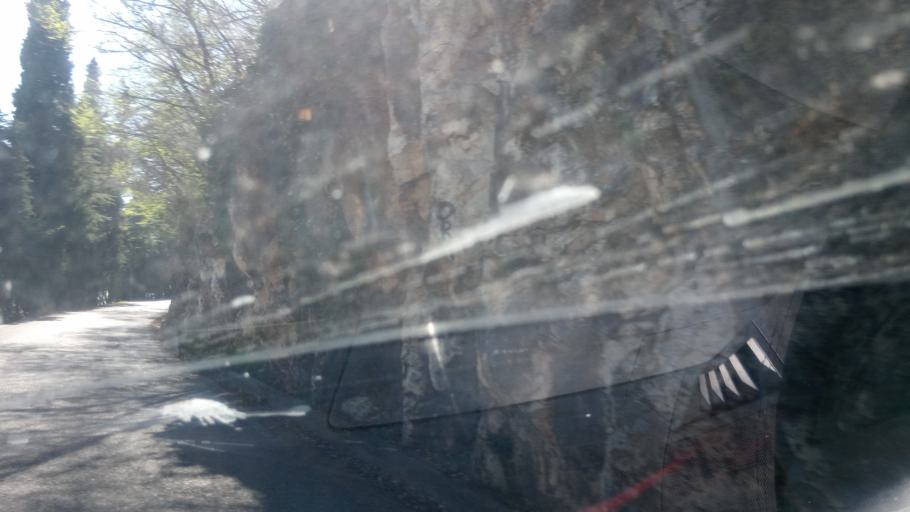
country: IT
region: Veneto
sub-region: Provincia di Treviso
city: Borso del Grappa
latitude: 45.8155
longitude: 11.7658
